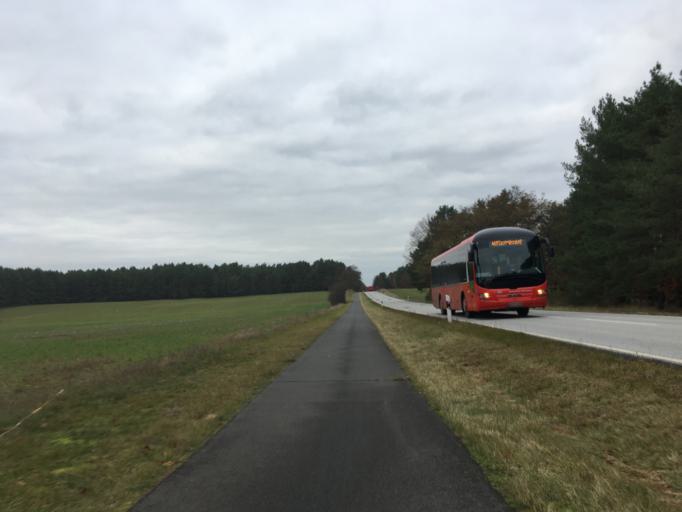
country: DE
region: Brandenburg
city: Mixdorf
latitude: 52.1989
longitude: 14.4590
